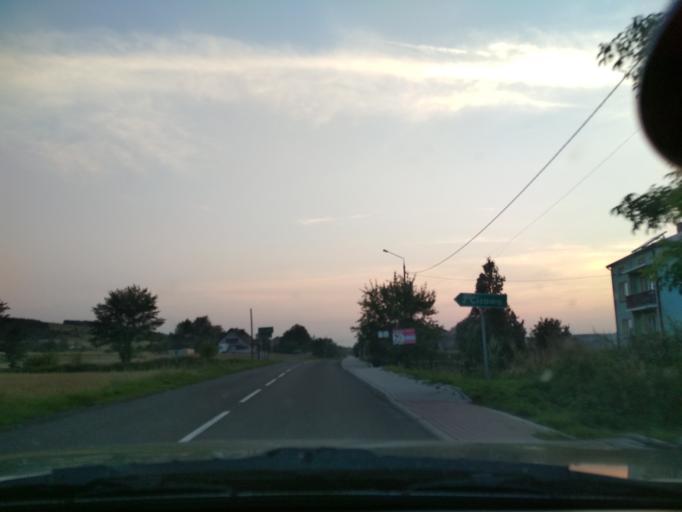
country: PL
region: Silesian Voivodeship
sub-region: Powiat zawiercianski
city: Pilica
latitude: 50.4705
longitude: 19.7346
